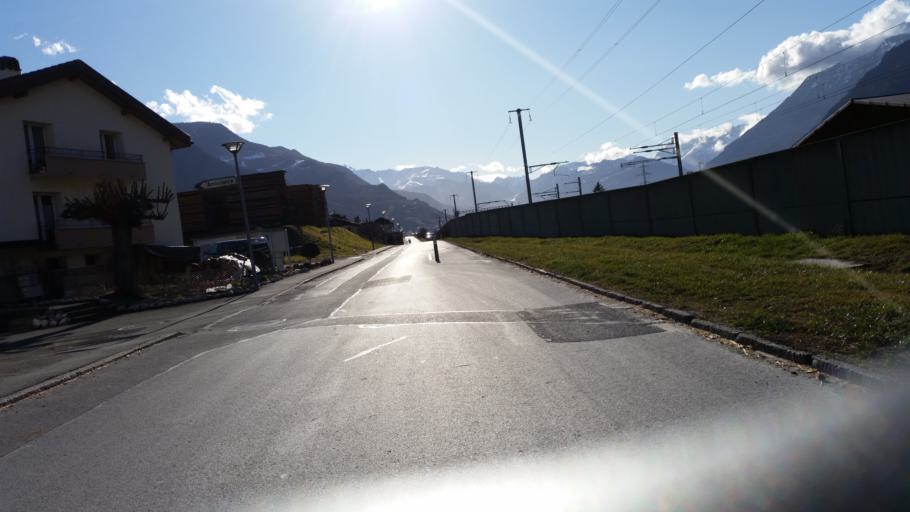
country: CH
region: Valais
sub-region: Martigny District
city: Riddes
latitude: 46.1769
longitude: 7.2240
